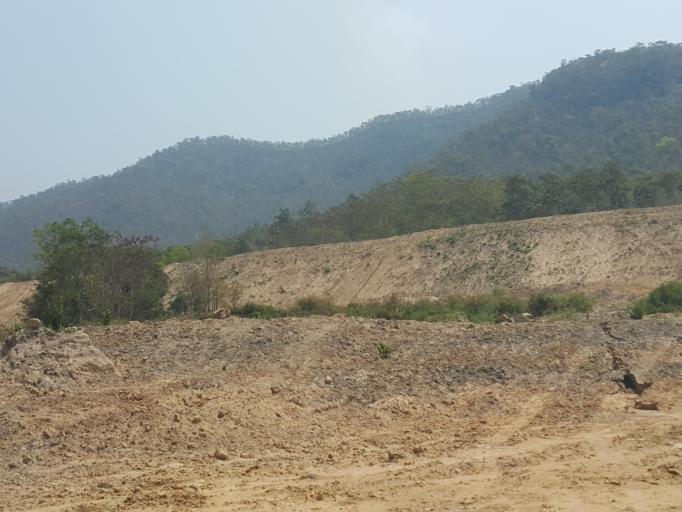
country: TH
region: Chiang Mai
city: Mae On
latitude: 18.7009
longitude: 99.2047
